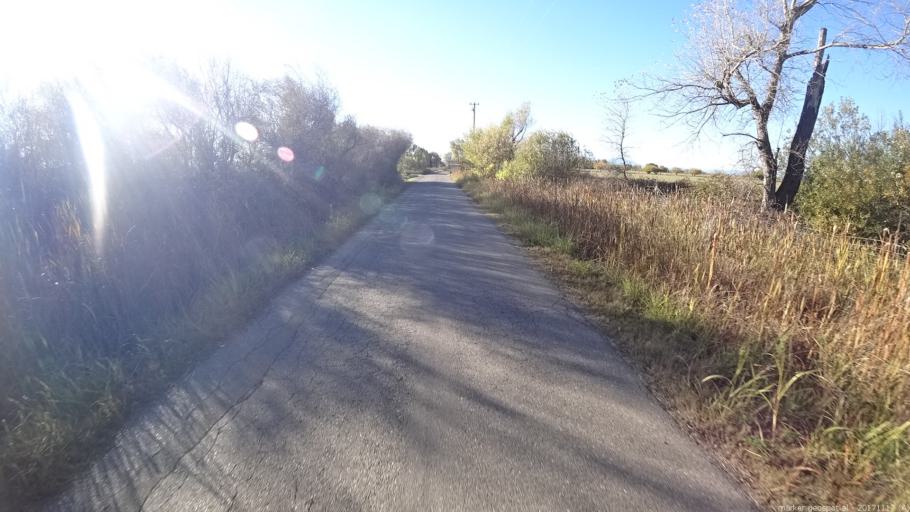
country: US
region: California
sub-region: Shasta County
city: Cottonwood
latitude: 40.3975
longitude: -122.2064
